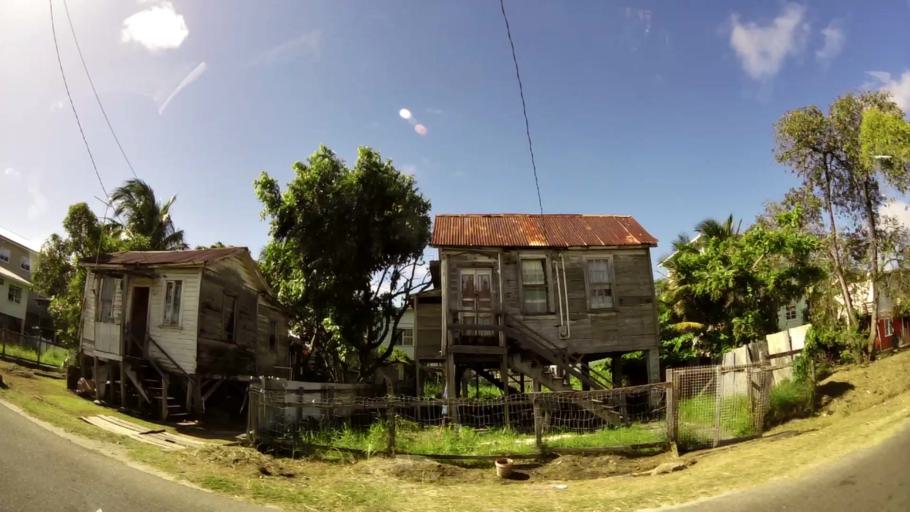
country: GY
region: Demerara-Mahaica
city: Georgetown
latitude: 6.8226
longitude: -58.1416
